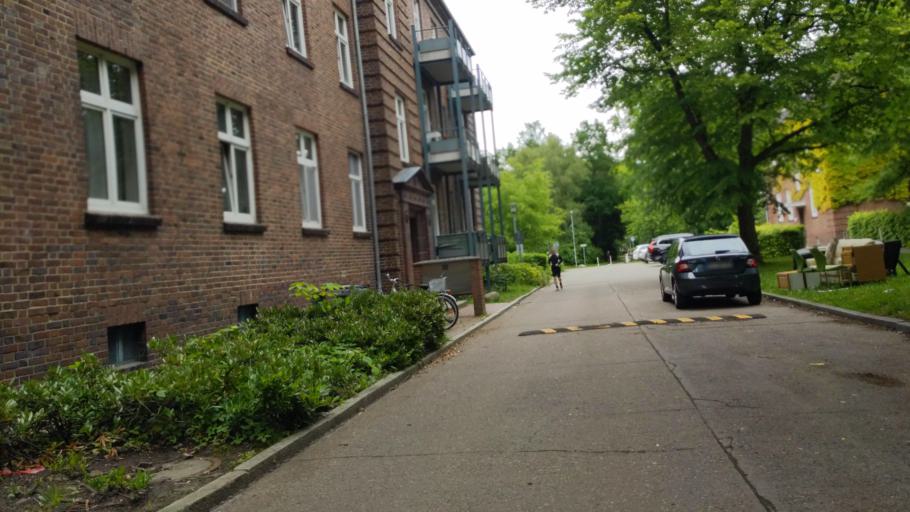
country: DE
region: Schleswig-Holstein
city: Luebeck
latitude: 53.8928
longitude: 10.6858
